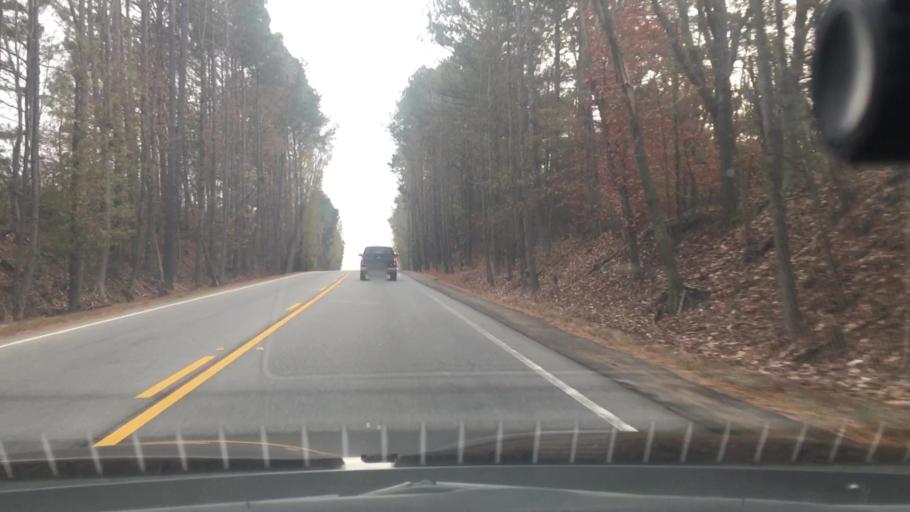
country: US
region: Georgia
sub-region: Coweta County
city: Senoia
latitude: 33.2560
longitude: -84.4952
